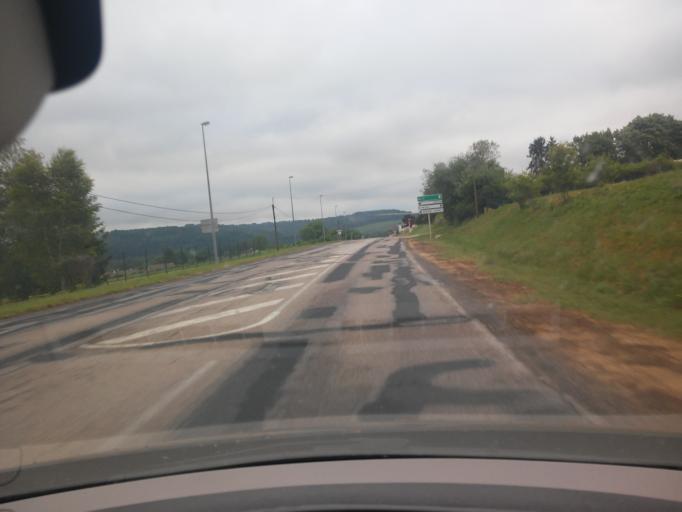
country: FR
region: Lorraine
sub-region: Departement de la Meuse
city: Saint-Mihiel
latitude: 48.9024
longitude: 5.5150
